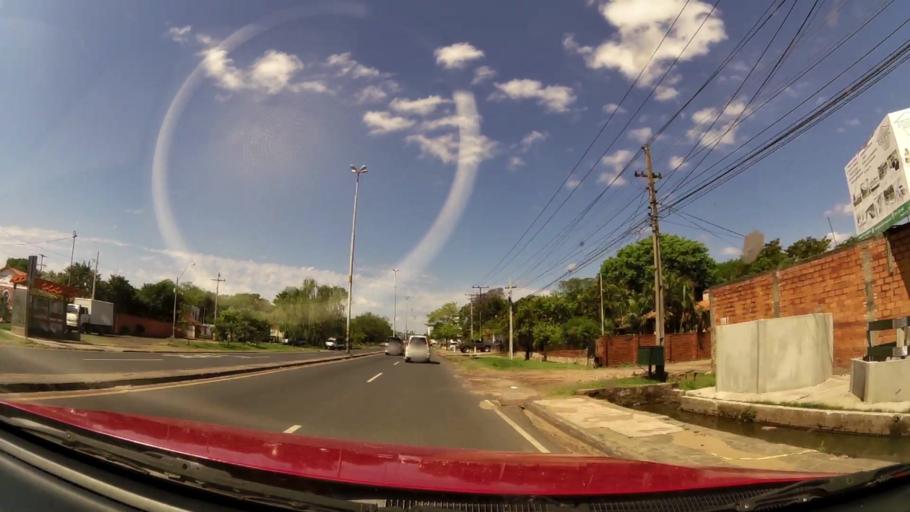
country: PY
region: Central
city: Colonia Mariano Roque Alonso
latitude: -25.2517
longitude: -57.5568
